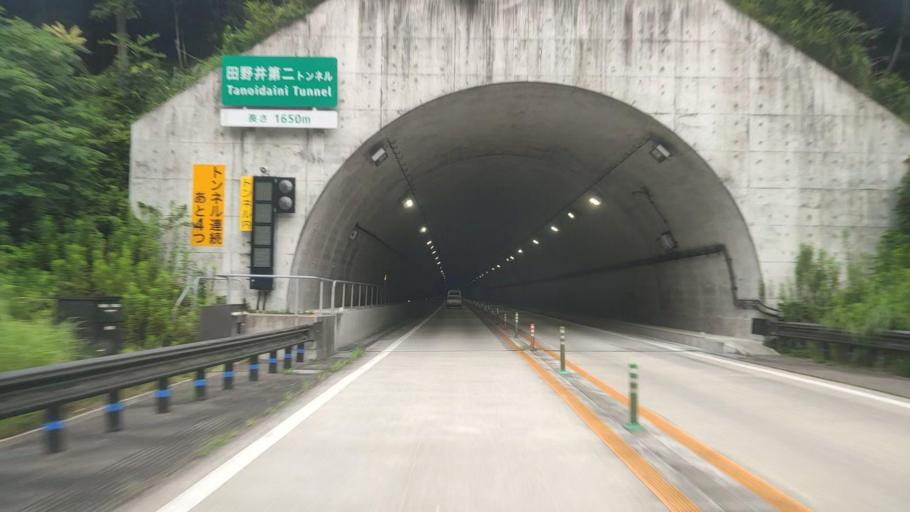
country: JP
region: Wakayama
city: Tanabe
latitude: 33.5863
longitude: 135.4464
